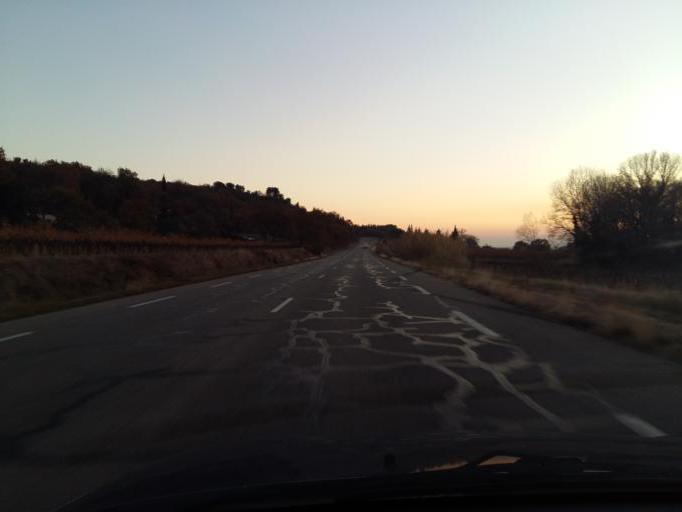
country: FR
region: Provence-Alpes-Cote d'Azur
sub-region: Departement du Vaucluse
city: Visan
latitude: 44.3319
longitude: 4.9471
